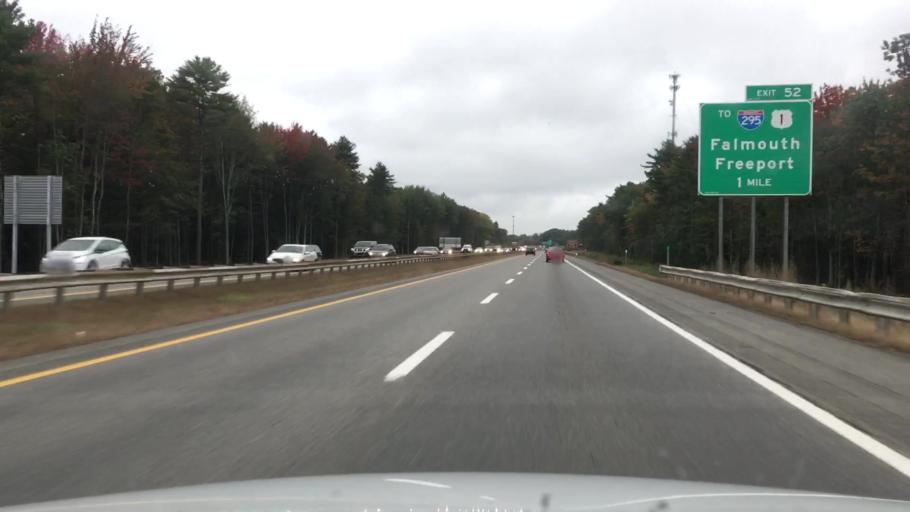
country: US
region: Maine
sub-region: Cumberland County
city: Westbrook
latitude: 43.7029
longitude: -70.3137
